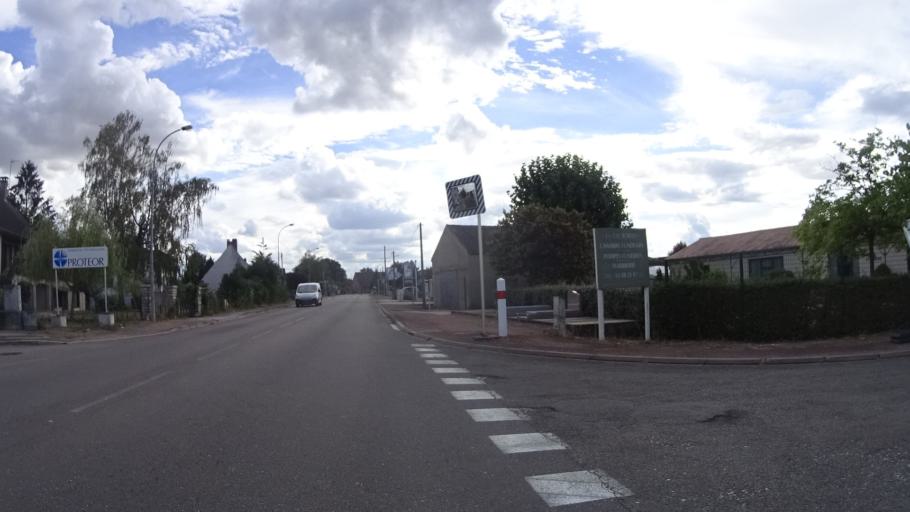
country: FR
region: Bourgogne
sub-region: Departement de la Cote-d'Or
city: Seurre
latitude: 47.0055
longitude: 5.1514
